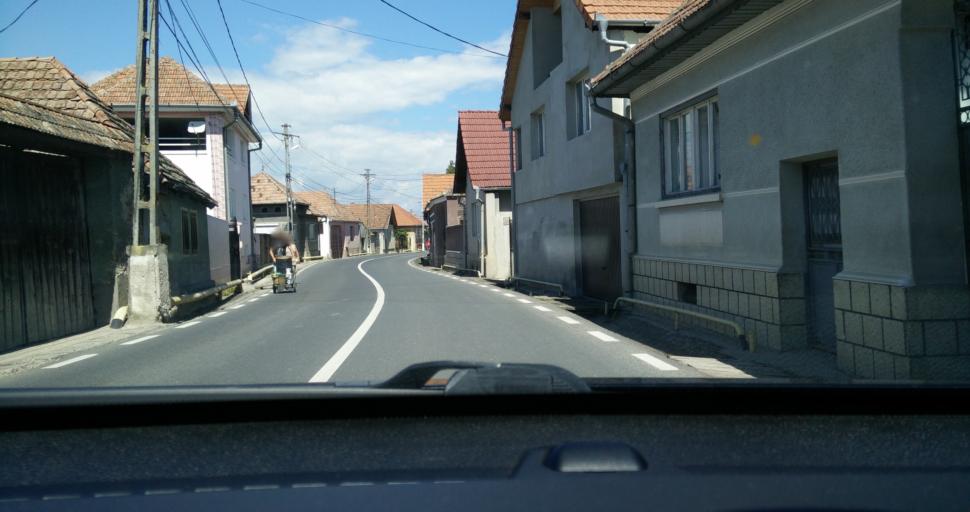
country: RO
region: Alba
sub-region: Comuna Sasciori
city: Sebesel
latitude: 45.8883
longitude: 23.5637
